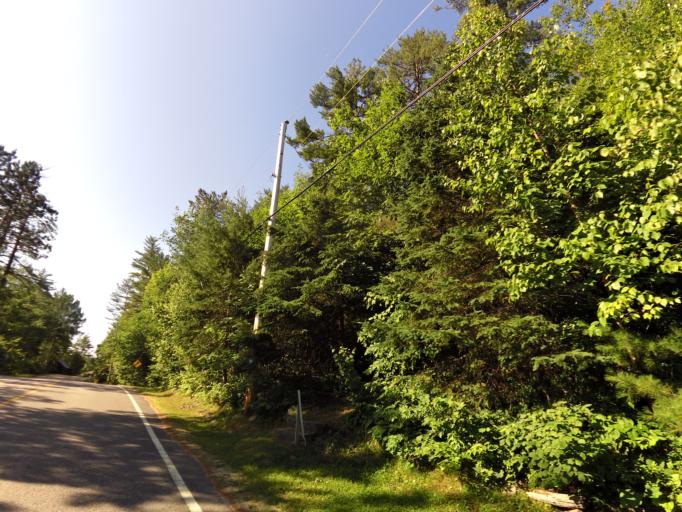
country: CA
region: Ontario
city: Deep River
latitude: 46.1987
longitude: -77.6838
